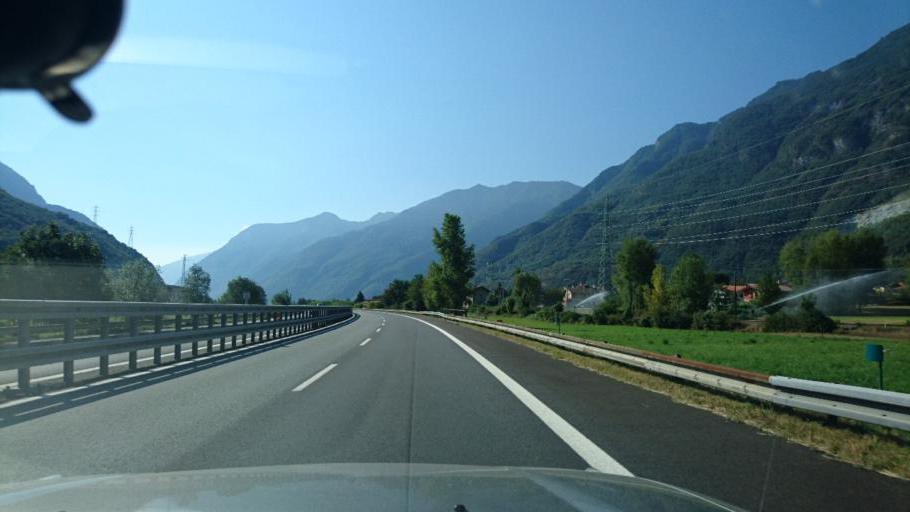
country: IT
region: Aosta Valley
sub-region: Valle d'Aosta
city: Champdepraz
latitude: 45.6877
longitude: 7.6676
